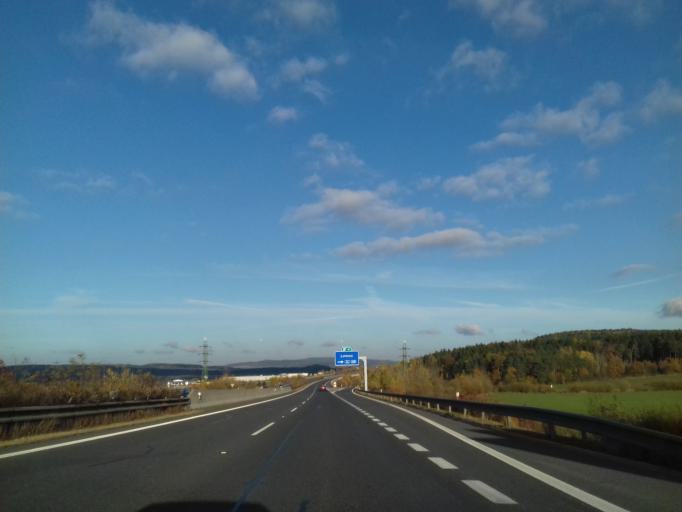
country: CZ
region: Plzensky
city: Stary Plzenec
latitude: 49.7318
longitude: 13.5018
